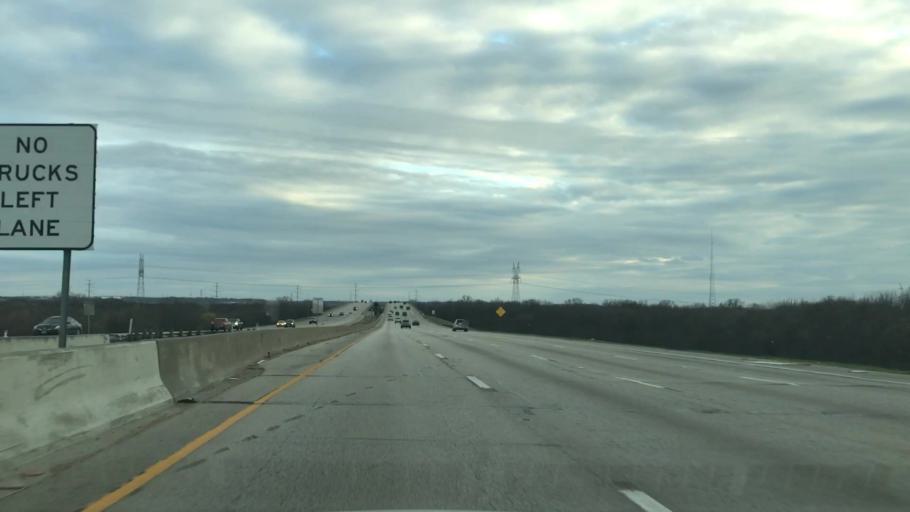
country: US
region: Texas
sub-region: Dallas County
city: Irving
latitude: 32.7931
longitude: -96.9204
